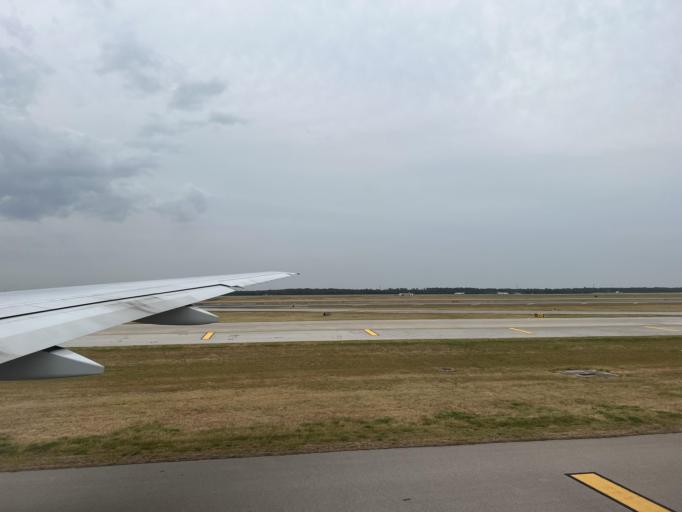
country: US
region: Texas
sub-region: Harris County
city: Aldine
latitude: 29.9908
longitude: -95.3455
